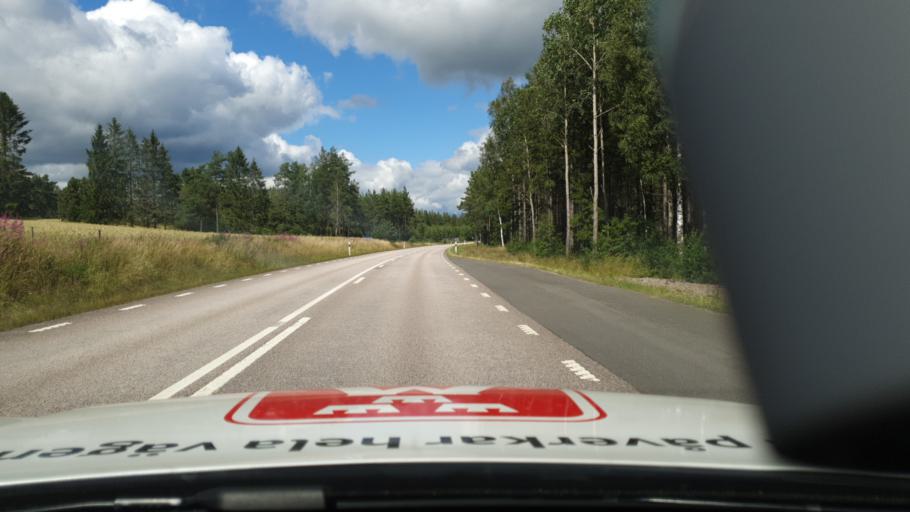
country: SE
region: Vaestra Goetaland
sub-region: Hjo Kommun
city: Hjo
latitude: 58.1876
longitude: 14.2028
